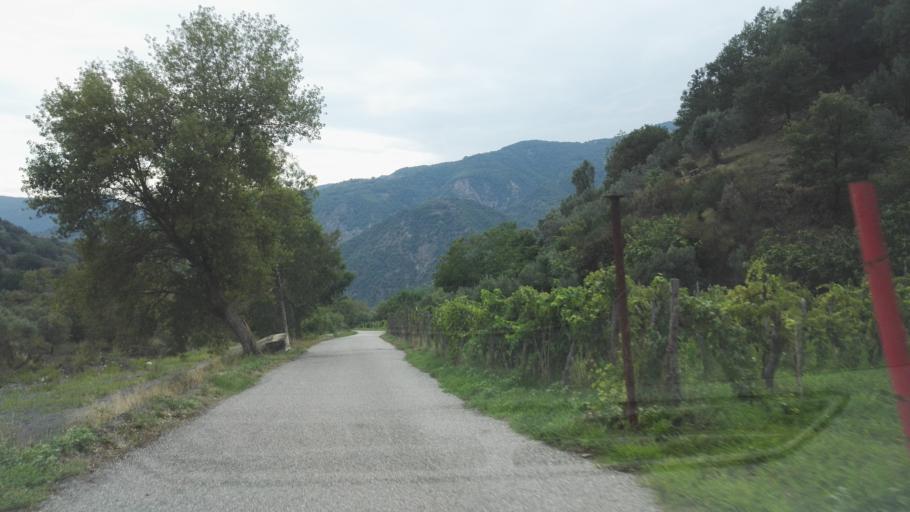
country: IT
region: Calabria
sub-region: Provincia di Reggio Calabria
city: Caulonia
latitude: 38.4288
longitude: 16.3923
